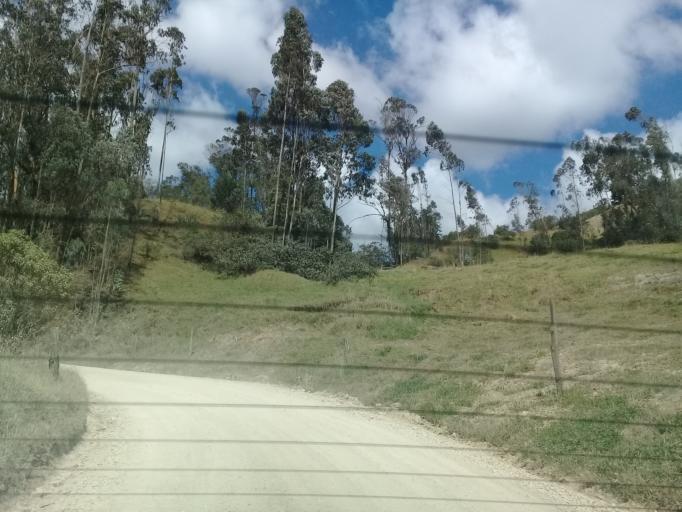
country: CO
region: Cundinamarca
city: Choconta
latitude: 5.1592
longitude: -73.7082
